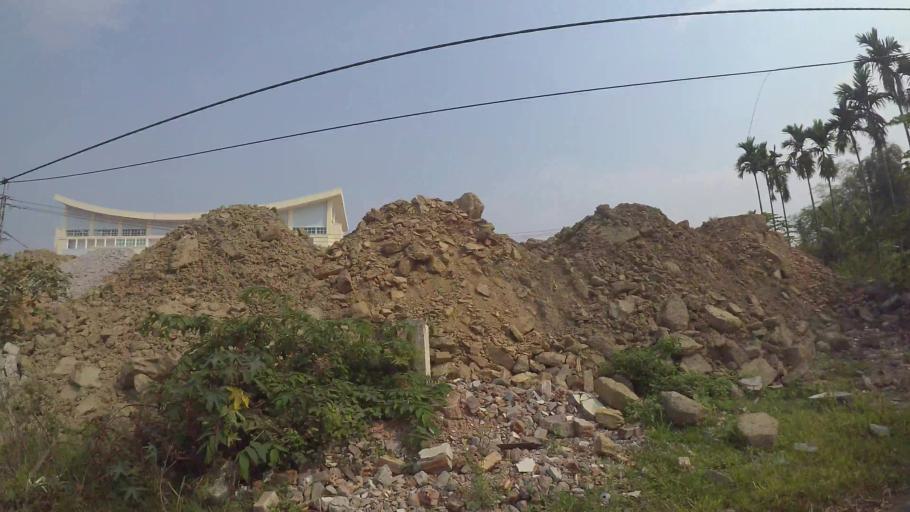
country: VN
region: Da Nang
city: Cam Le
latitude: 15.9967
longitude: 108.2187
